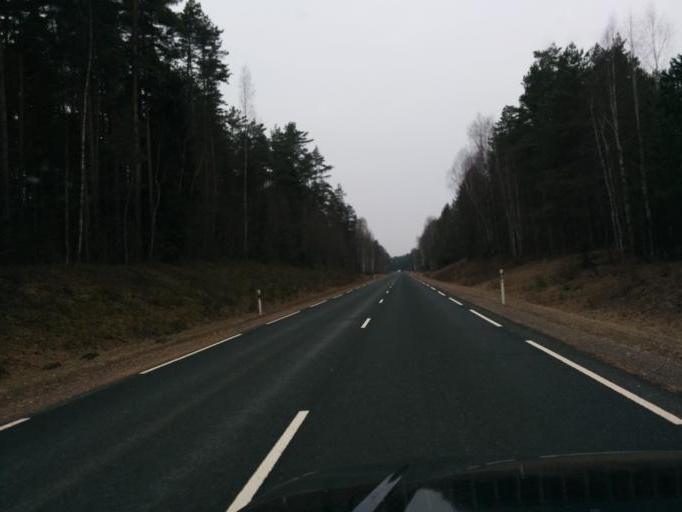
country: LV
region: Ogre
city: Ogre
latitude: 56.7929
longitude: 24.6014
